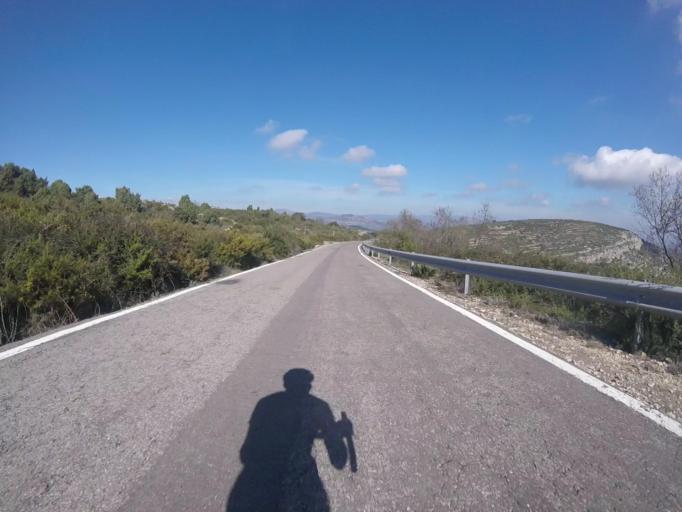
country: ES
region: Valencia
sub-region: Provincia de Castello
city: Albocasser
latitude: 40.3416
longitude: 0.0501
